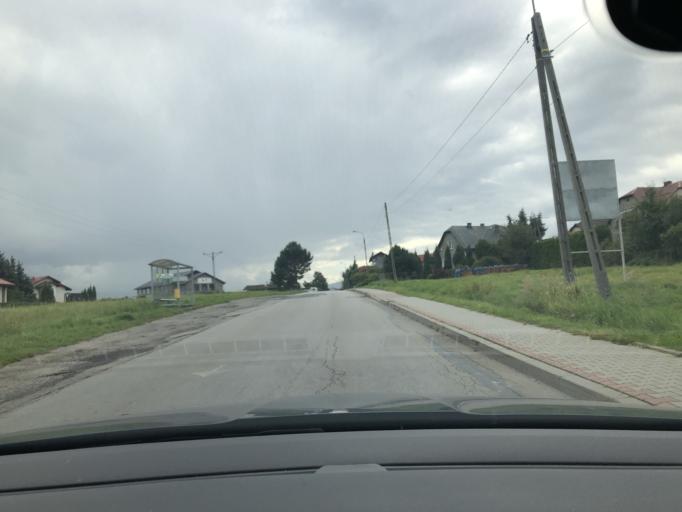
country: PL
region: Silesian Voivodeship
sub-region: Powiat zywiecki
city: Zarzecze
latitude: 49.7213
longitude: 19.1770
